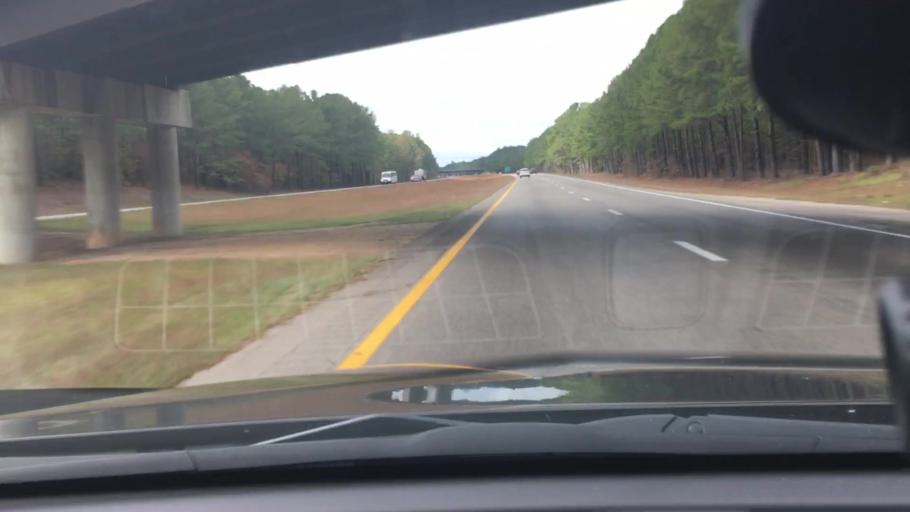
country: US
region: North Carolina
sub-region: Wilson County
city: Lucama
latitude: 35.7823
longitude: -78.0870
